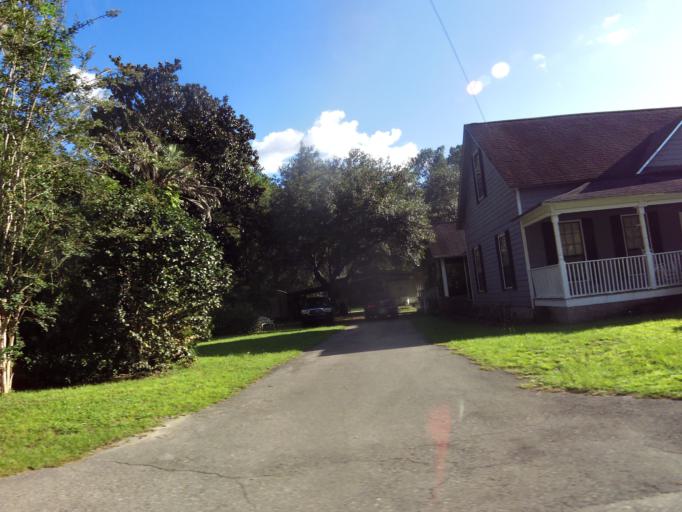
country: US
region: Florida
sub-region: Wakulla County
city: Crawfordville
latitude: 30.0608
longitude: -84.4946
